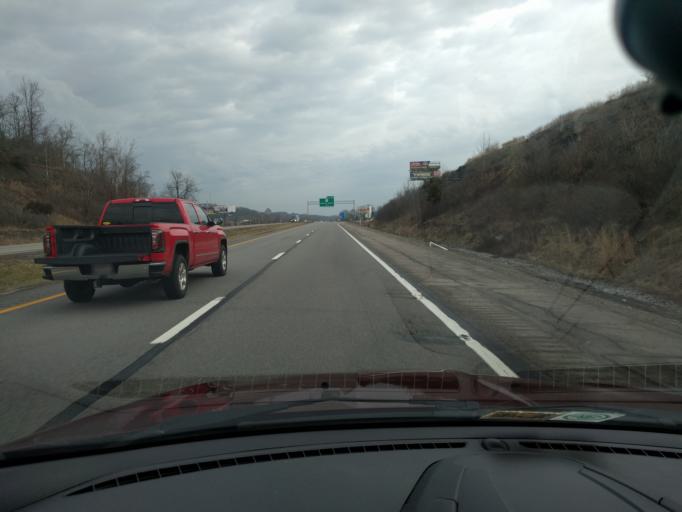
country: US
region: West Virginia
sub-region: Wood County
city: Mineral Wells
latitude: 39.1678
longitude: -81.5396
